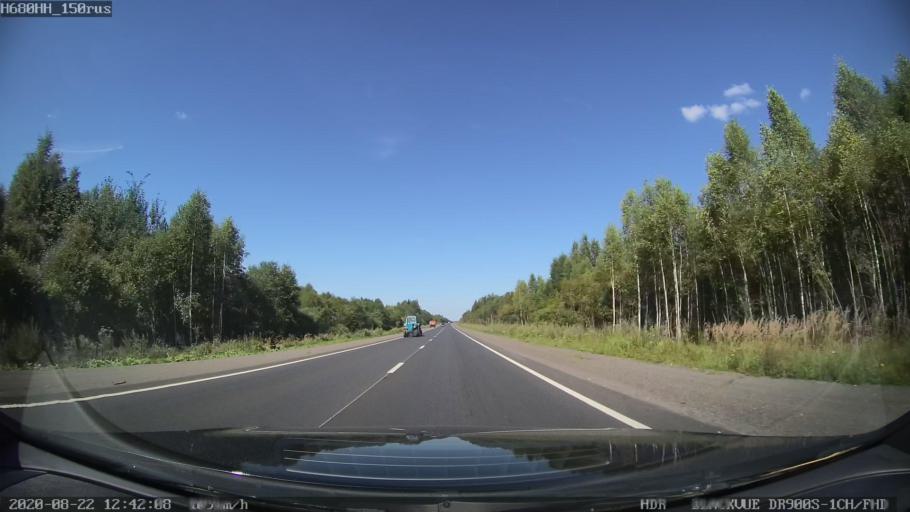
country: RU
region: Tverskaya
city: Rameshki
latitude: 57.3574
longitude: 36.0960
